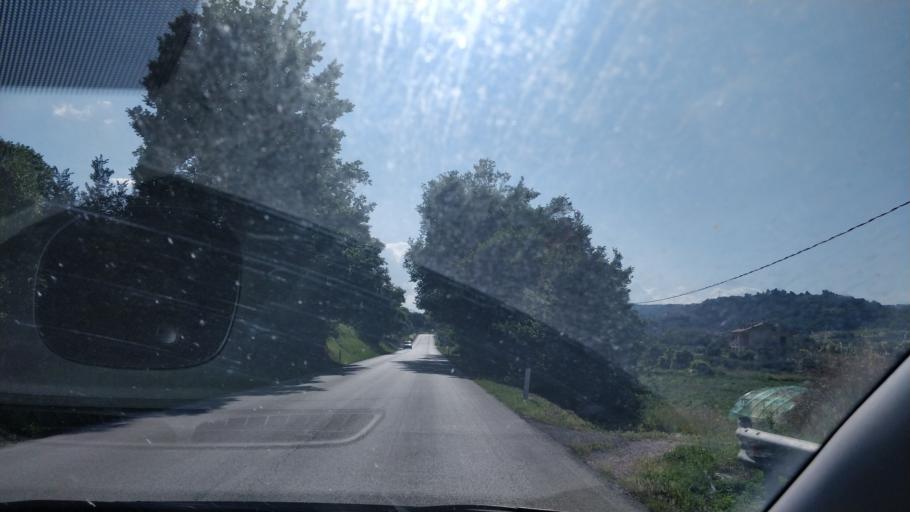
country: IT
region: The Marches
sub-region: Provincia di Ascoli Piceno
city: Cupra Marittima
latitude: 43.0356
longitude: 13.8419
